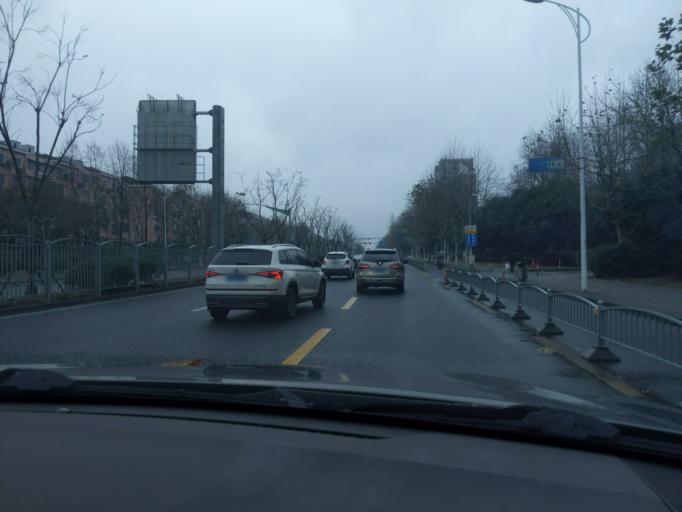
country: CN
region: Shanghai Shi
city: Huamu
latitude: 31.1895
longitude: 121.5226
